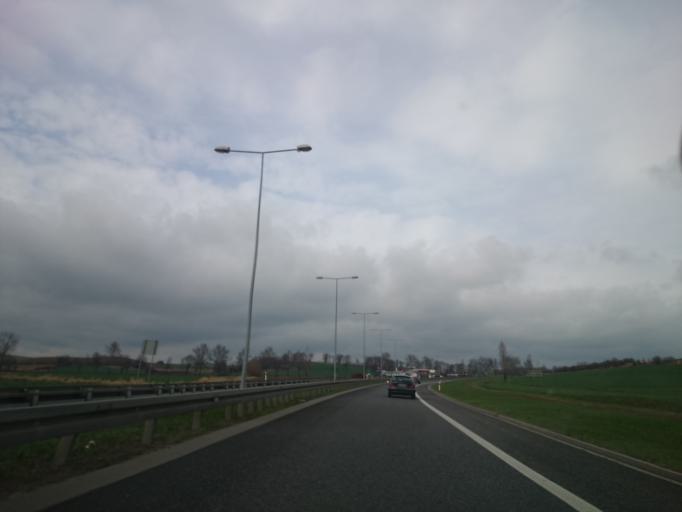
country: PL
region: Opole Voivodeship
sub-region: Powiat nyski
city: Otmuchow
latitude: 50.4631
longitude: 17.1976
